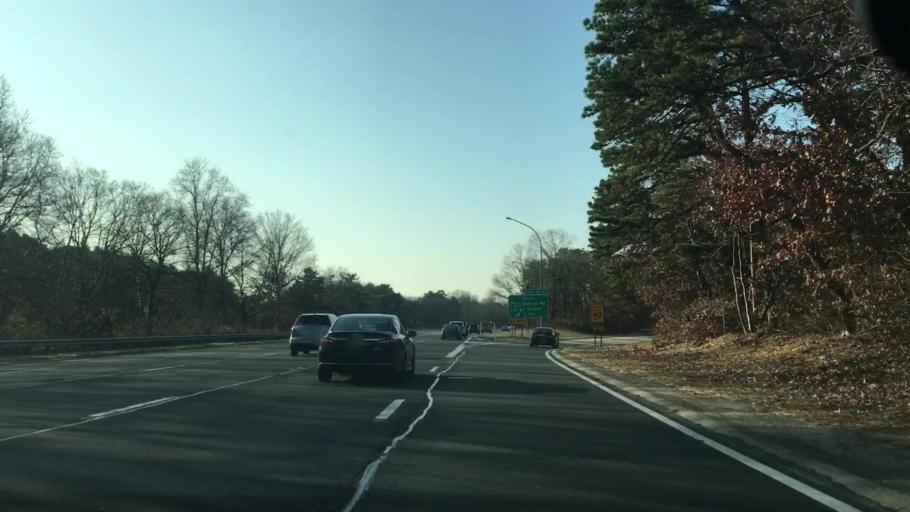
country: US
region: New York
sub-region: Suffolk County
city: Bay Wood
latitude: 40.7414
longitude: -73.2825
